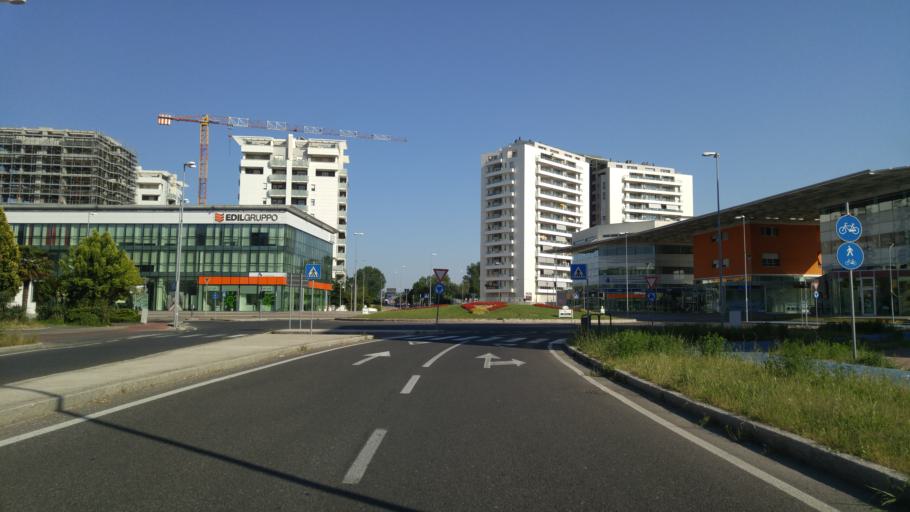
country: IT
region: The Marches
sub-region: Provincia di Pesaro e Urbino
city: Pesaro
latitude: 43.9056
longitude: 12.8892
